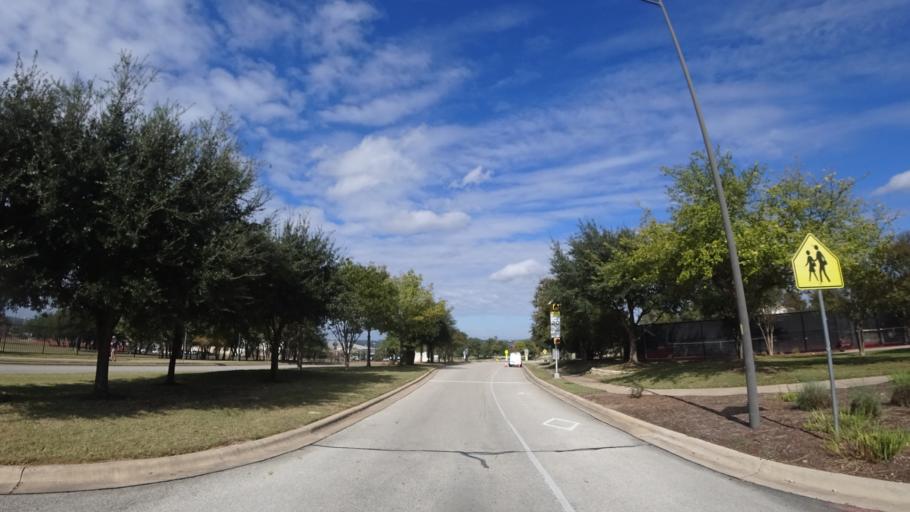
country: US
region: Texas
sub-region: Travis County
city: Hudson Bend
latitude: 30.3641
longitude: -97.9008
